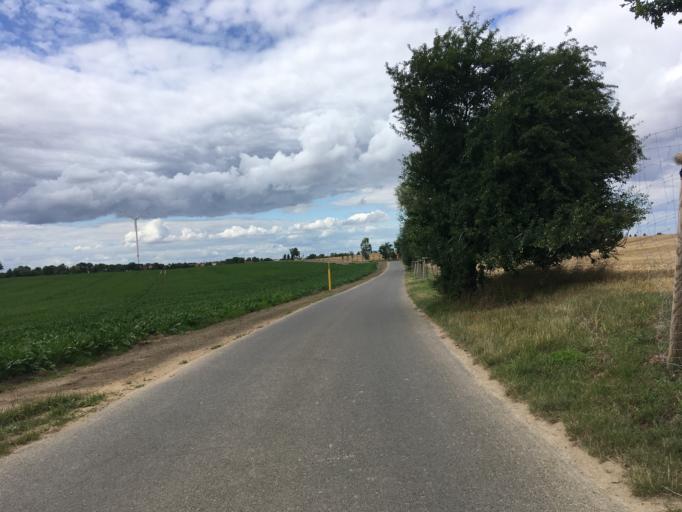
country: DE
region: Brandenburg
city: Gramzow
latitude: 53.2635
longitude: 14.0171
